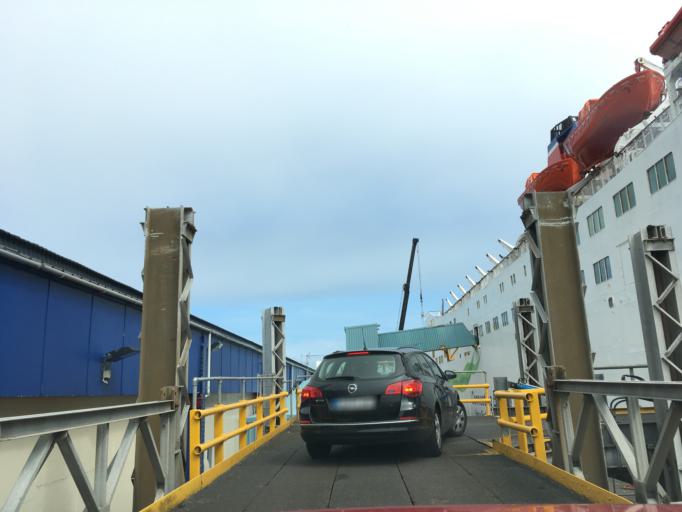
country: GB
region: Wales
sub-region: Pembrokeshire
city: Goodwick
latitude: 52.0102
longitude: -4.9861
